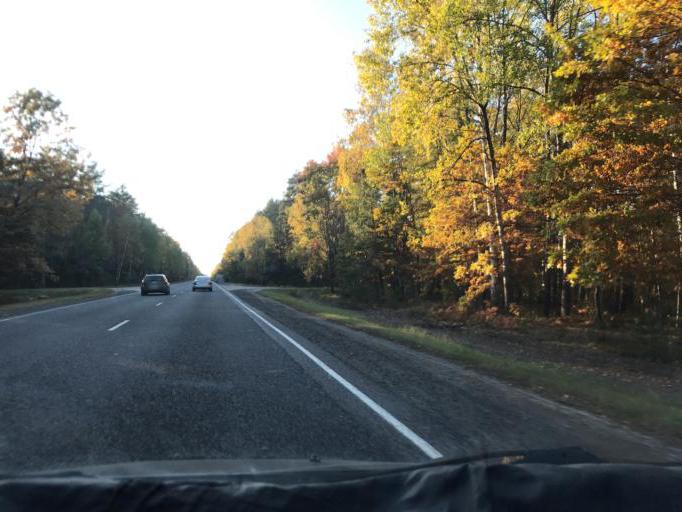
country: BY
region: Gomel
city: Zhytkavichy
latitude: 52.2731
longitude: 28.0955
